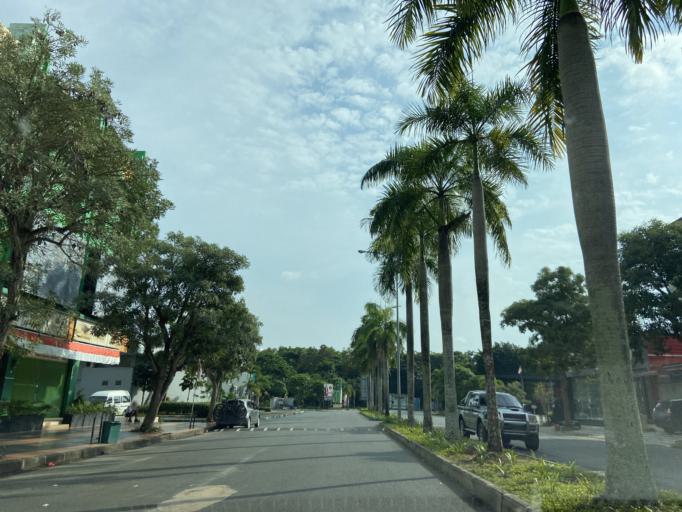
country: SG
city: Singapore
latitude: 1.1021
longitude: 104.0342
